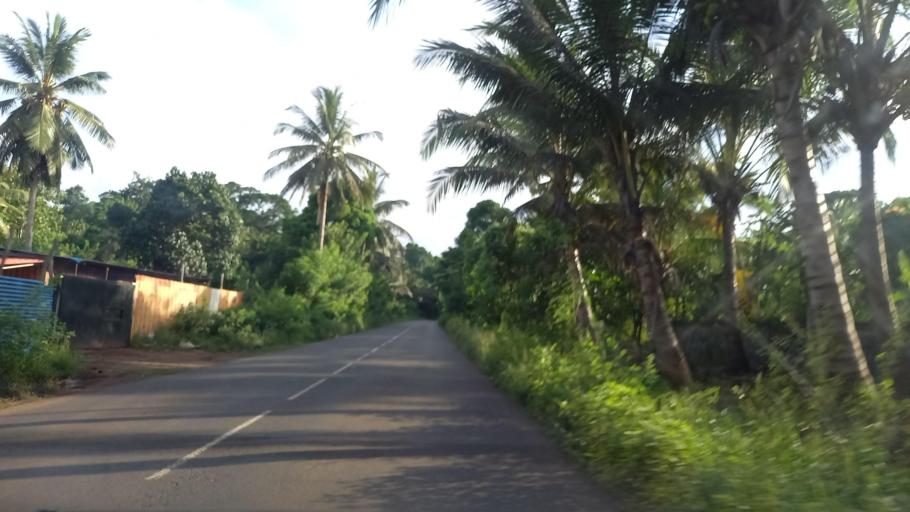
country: YT
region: Bandraboua
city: Bandraboua
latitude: -12.7306
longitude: 45.1197
